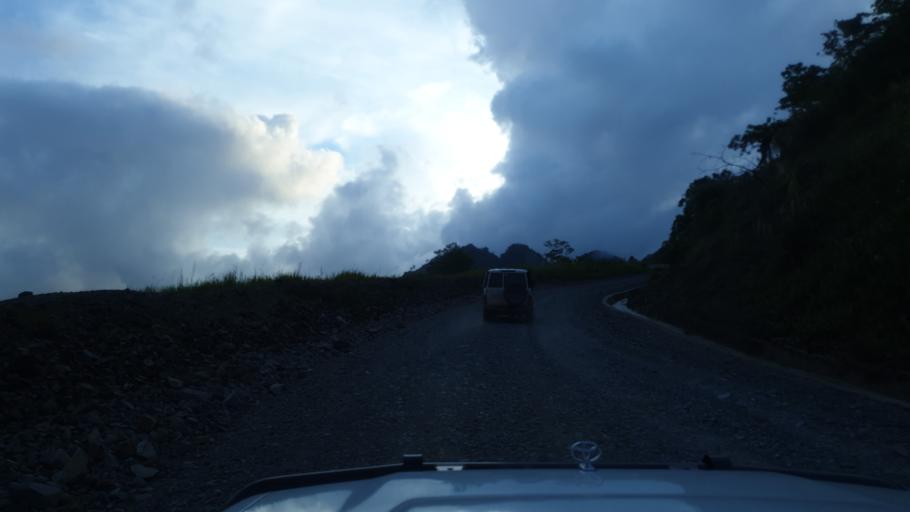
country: PG
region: Bougainville
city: Panguna
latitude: -6.3352
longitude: 155.4628
